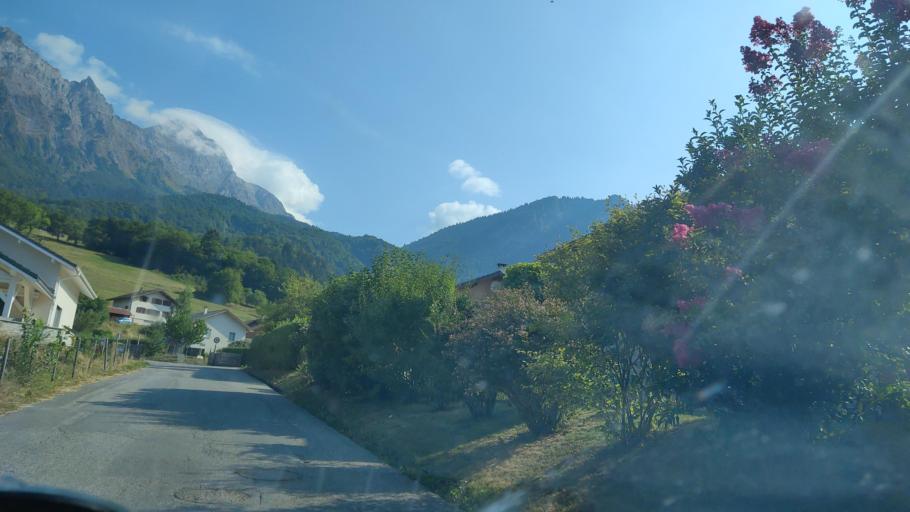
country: FR
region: Rhone-Alpes
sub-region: Departement de la Savoie
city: Ugine
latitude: 45.7609
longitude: 6.4086
